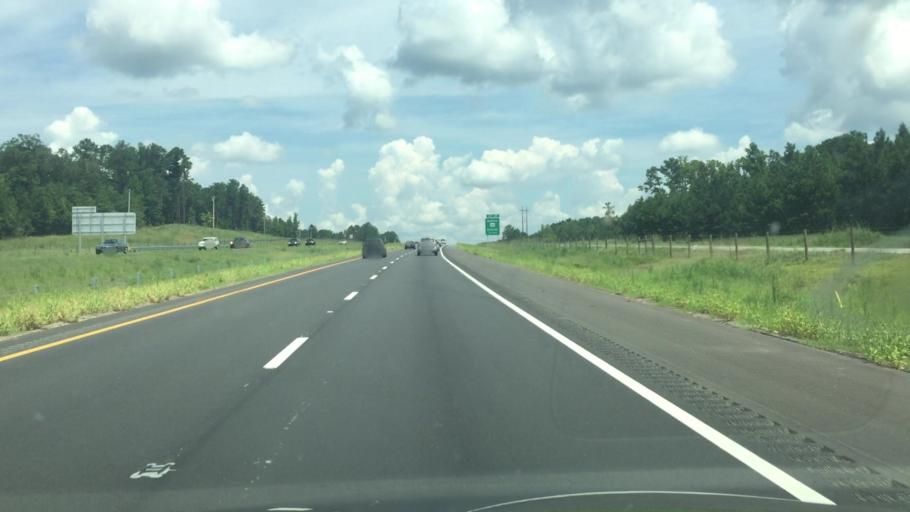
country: US
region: North Carolina
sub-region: Richmond County
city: Ellerbe
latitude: 35.0305
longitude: -79.7694
